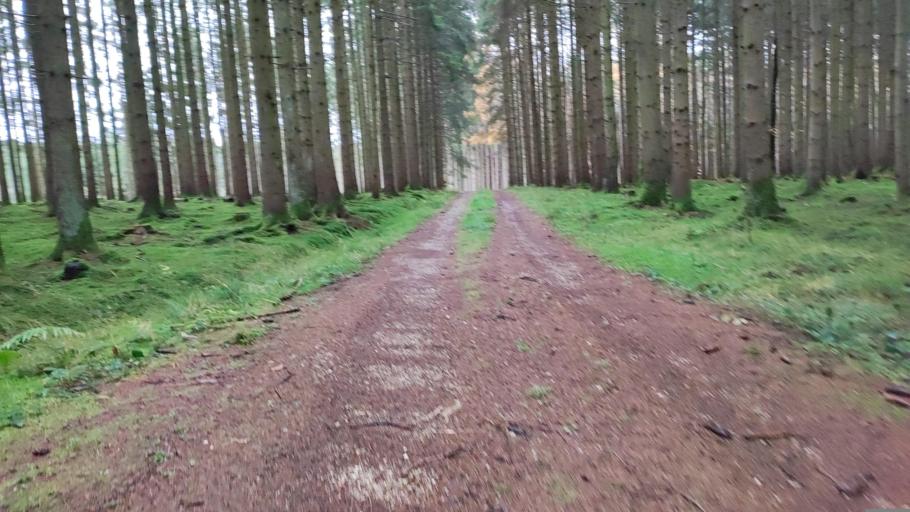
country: DE
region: Bavaria
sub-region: Swabia
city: Burtenbach
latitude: 48.3650
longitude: 10.5179
